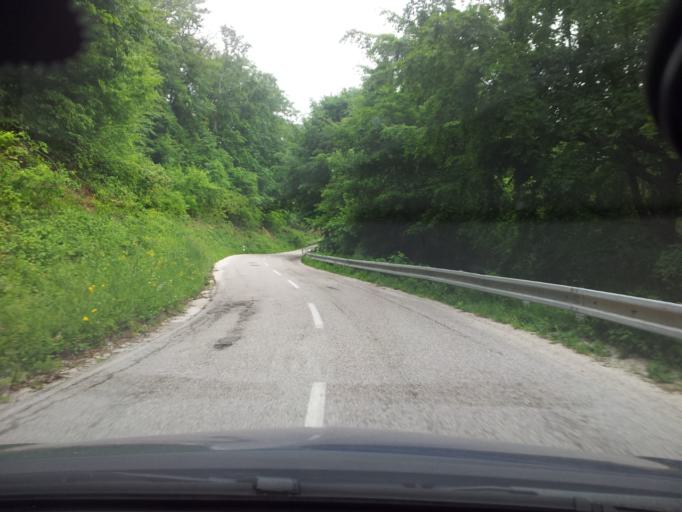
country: SK
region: Nitriansky
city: Partizanske
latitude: 48.5702
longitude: 18.4568
